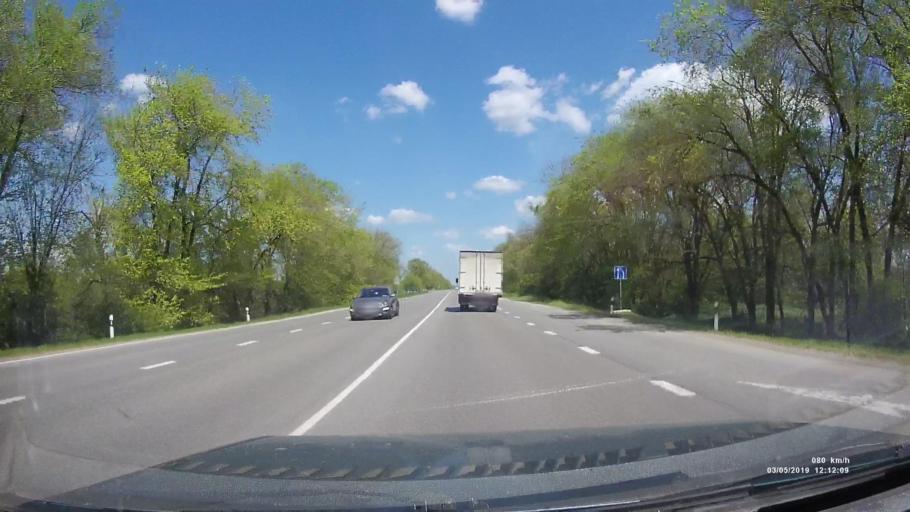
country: RU
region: Rostov
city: Bagayevskaya
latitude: 47.3183
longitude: 40.5442
